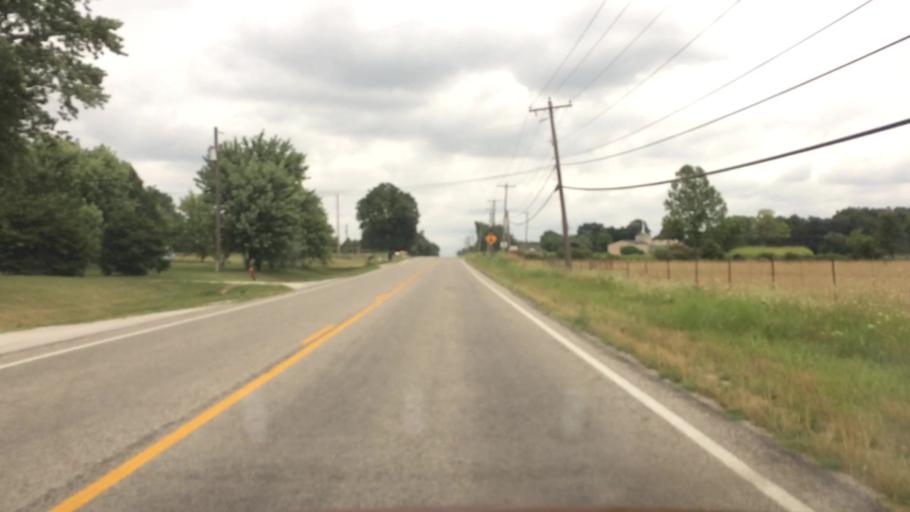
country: US
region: Missouri
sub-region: Greene County
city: Springfield
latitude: 37.2904
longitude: -93.2638
